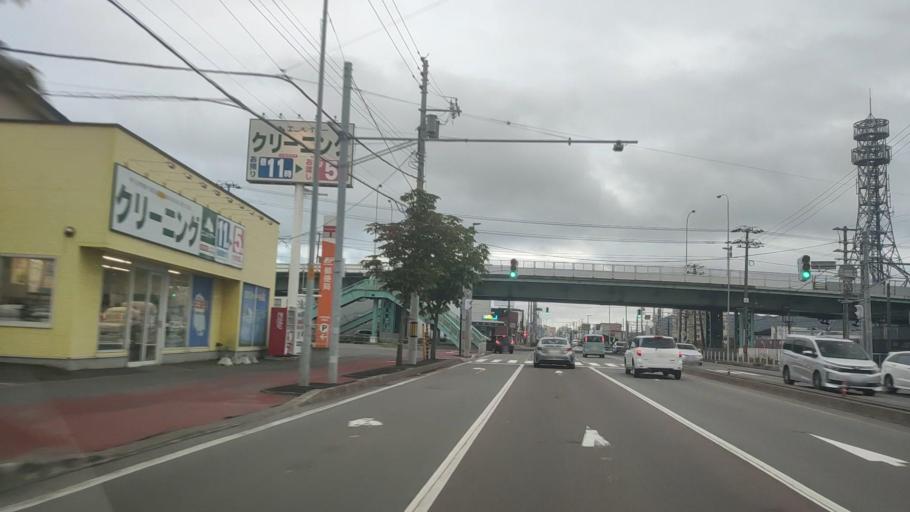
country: JP
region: Hokkaido
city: Hakodate
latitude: 41.8015
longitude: 140.7344
